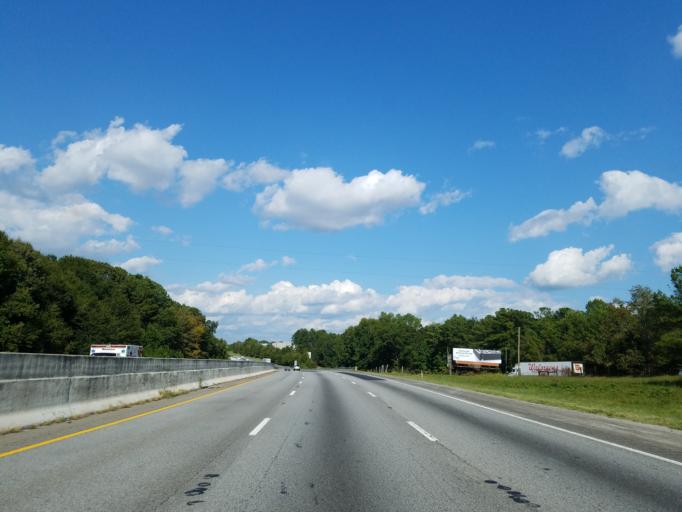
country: US
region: South Carolina
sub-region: Anderson County
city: Williamston
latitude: 34.6356
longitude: -82.5906
